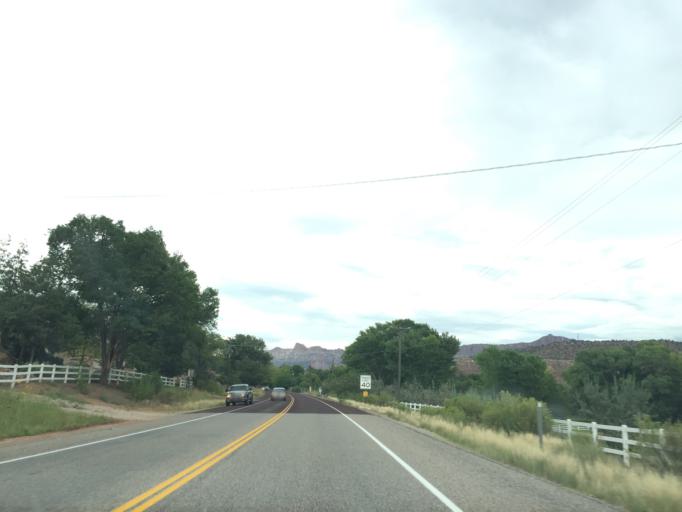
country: US
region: Utah
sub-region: Washington County
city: Hildale
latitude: 37.1610
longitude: -113.0518
